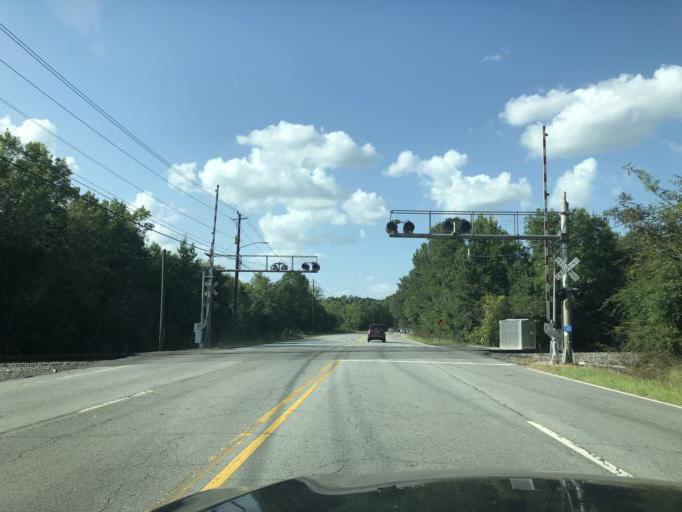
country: US
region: Georgia
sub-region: Muscogee County
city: Columbus
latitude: 32.5026
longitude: -84.8920
